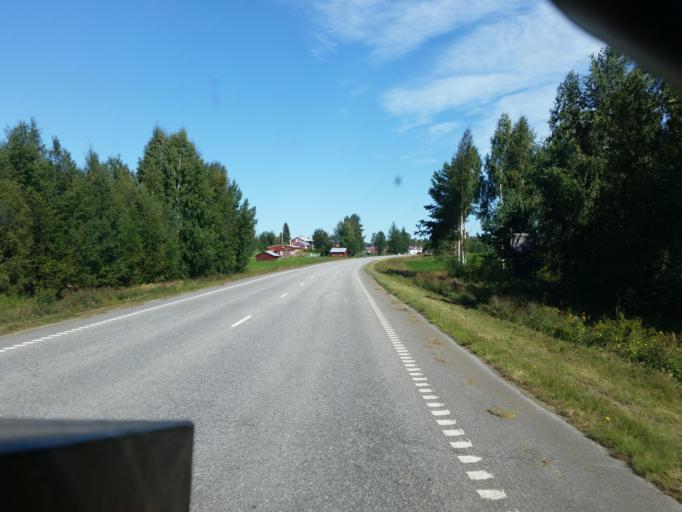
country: SE
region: Norrbotten
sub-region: Pitea Kommun
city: Roknas
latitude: 65.3349
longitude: 21.2284
